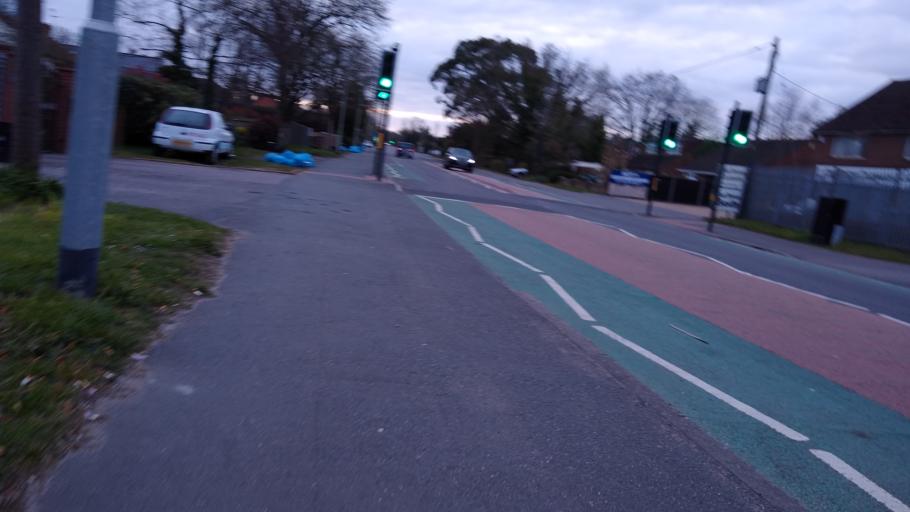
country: GB
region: England
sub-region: Wokingham
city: Winnersh
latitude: 51.4354
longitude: -0.8914
